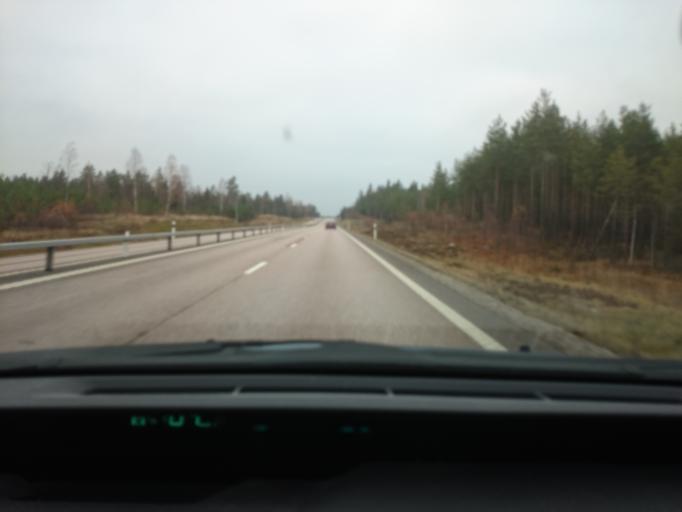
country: SE
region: Vaestmanland
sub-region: Sala Kommun
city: Sala
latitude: 59.9991
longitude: 16.4239
